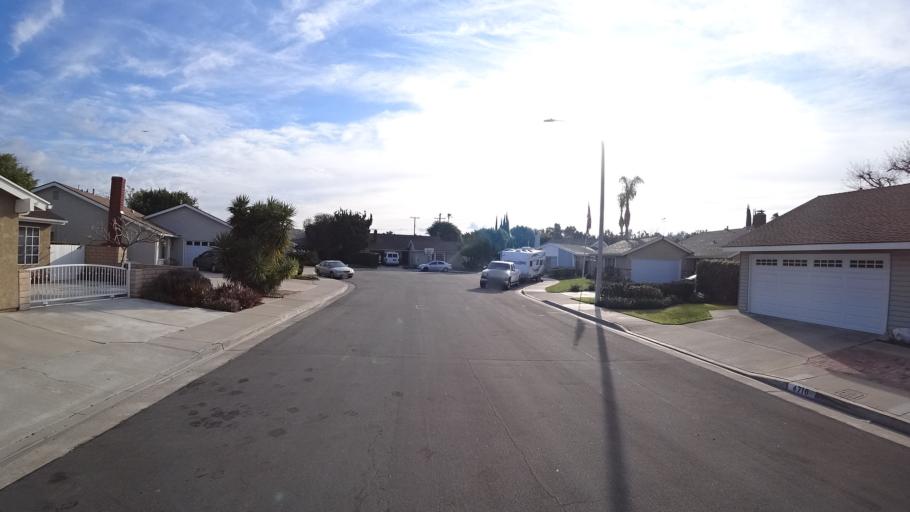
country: US
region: California
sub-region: Orange County
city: Yorba Linda
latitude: 33.8537
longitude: -117.8142
